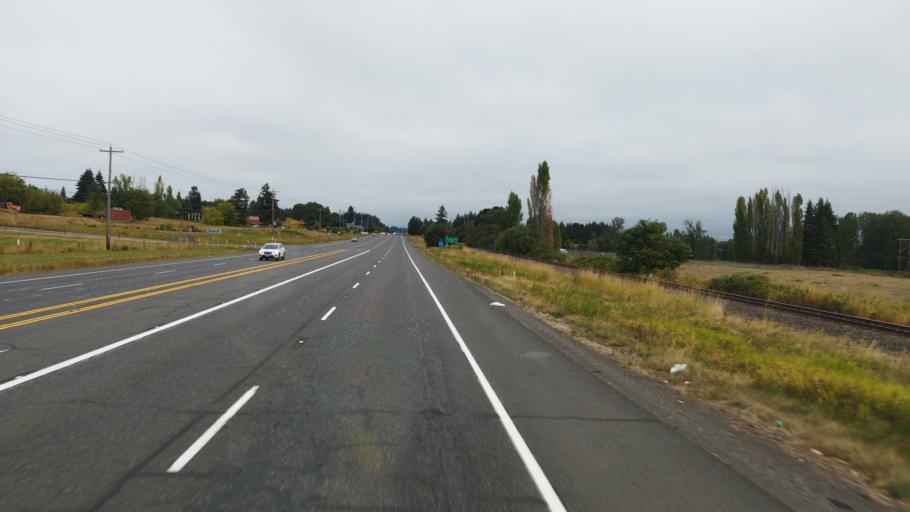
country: US
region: Oregon
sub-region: Columbia County
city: Warren
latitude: 45.8050
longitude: -122.8591
